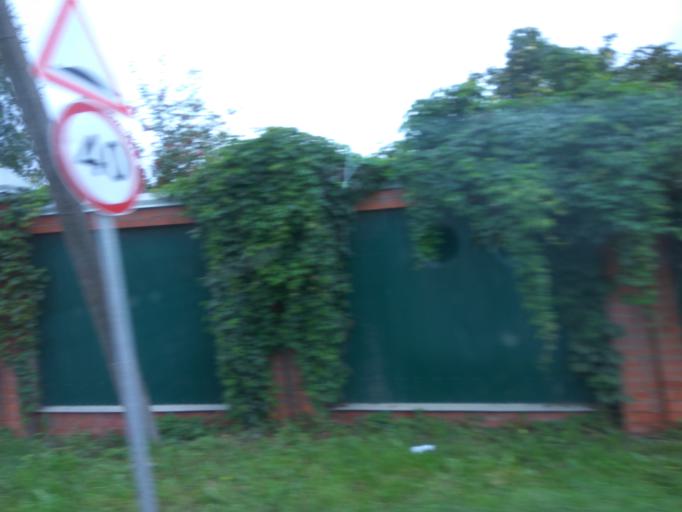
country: RU
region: Moskovskaya
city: Malyshevo
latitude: 55.5027
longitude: 38.3425
